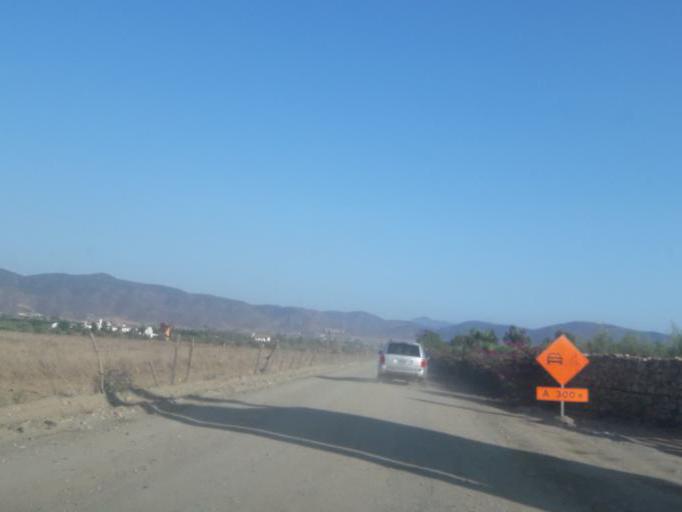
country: MX
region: Baja California
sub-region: Ensenada
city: Rancho Verde
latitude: 32.0902
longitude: -116.6295
